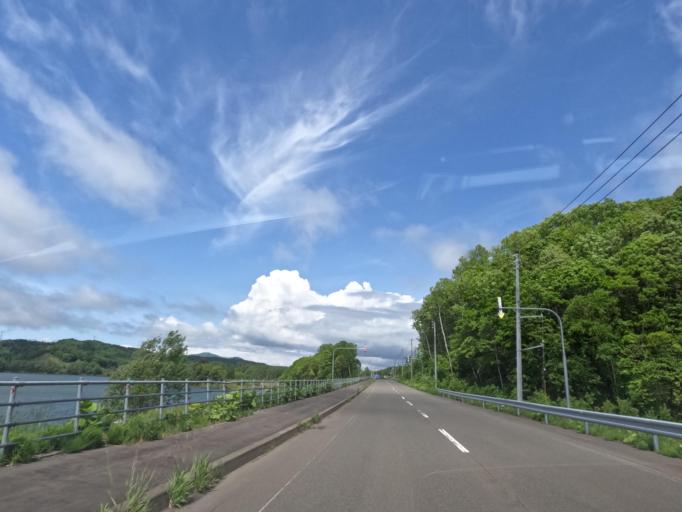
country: JP
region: Hokkaido
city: Tobetsu
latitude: 43.3646
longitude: 141.5719
